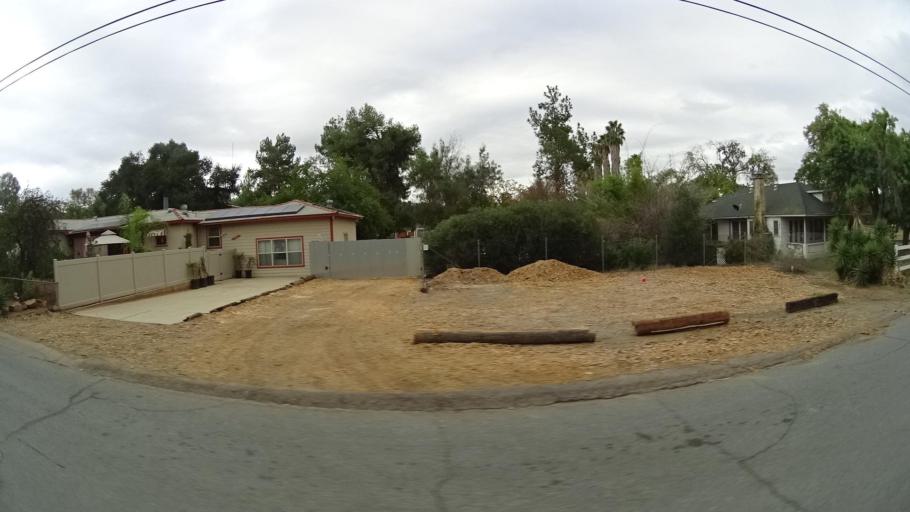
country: US
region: California
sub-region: San Diego County
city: Eucalyptus Hills
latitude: 32.8703
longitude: -116.9431
